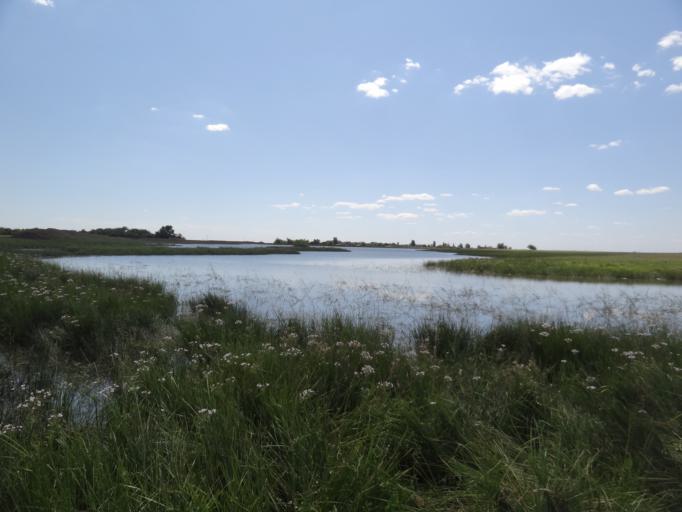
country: RU
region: Saratov
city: Sovetskoye
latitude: 51.2923
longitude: 46.6574
